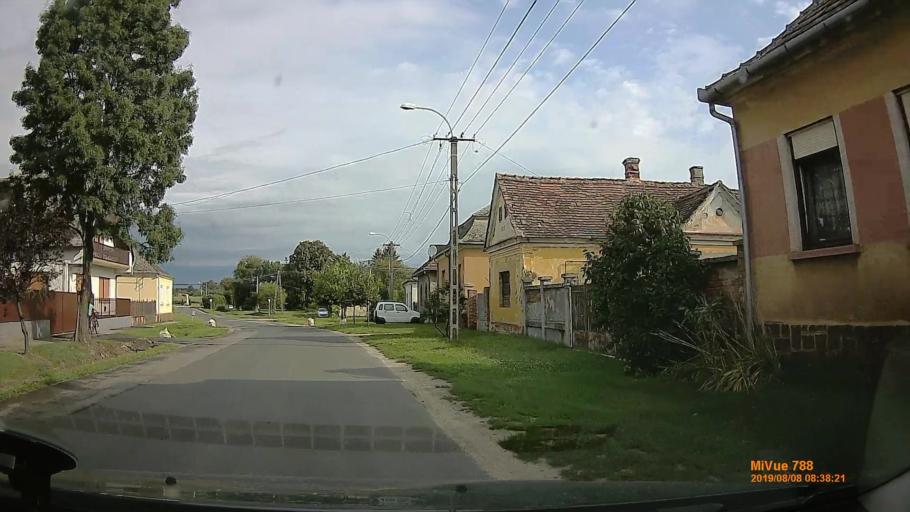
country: HU
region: Zala
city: Nagykanizsa
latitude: 46.4617
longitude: 16.9591
